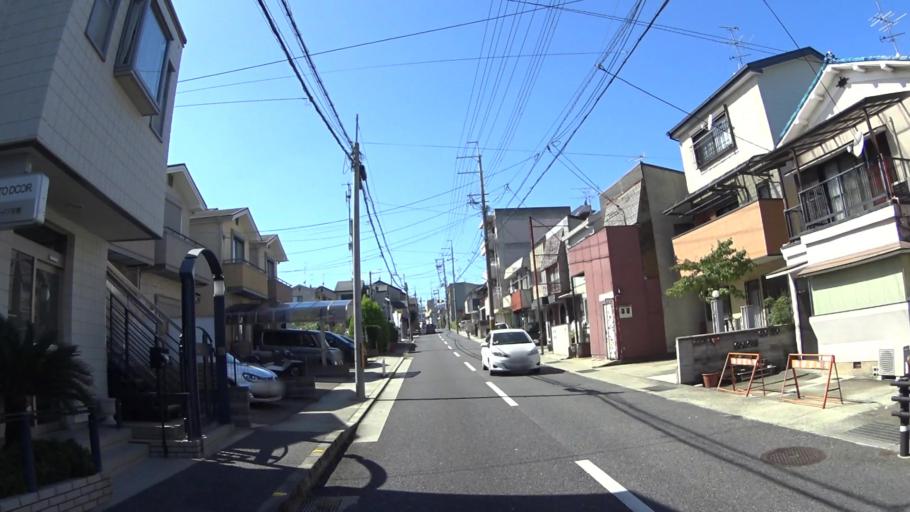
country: JP
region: Kyoto
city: Muko
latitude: 34.9465
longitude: 135.7042
